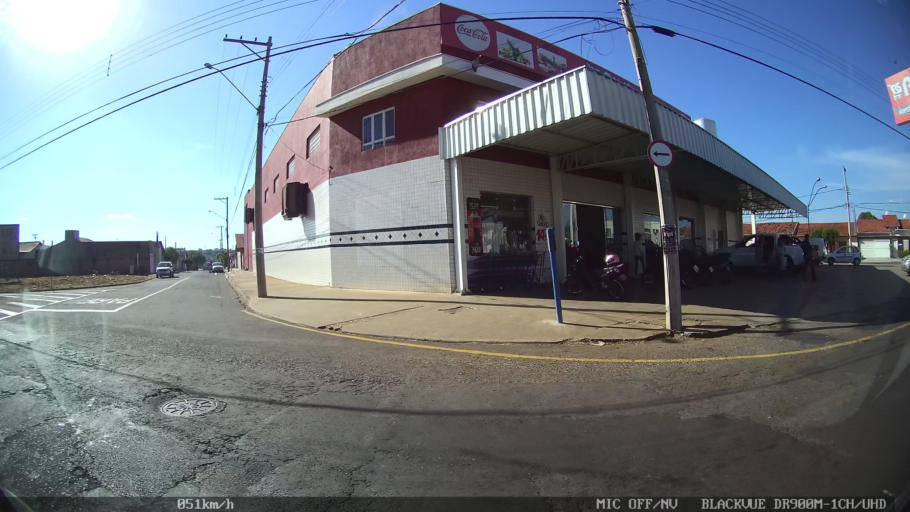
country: BR
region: Sao Paulo
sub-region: Franca
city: Franca
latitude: -20.4875
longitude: -47.4142
